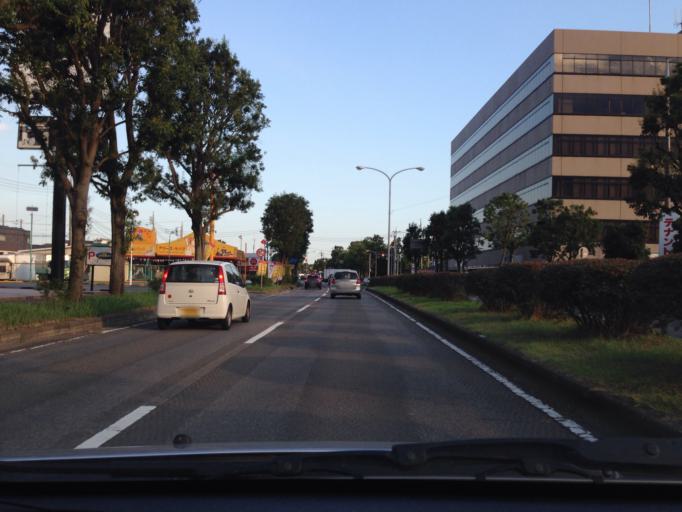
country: JP
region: Ibaraki
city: Naka
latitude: 36.0470
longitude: 140.1505
